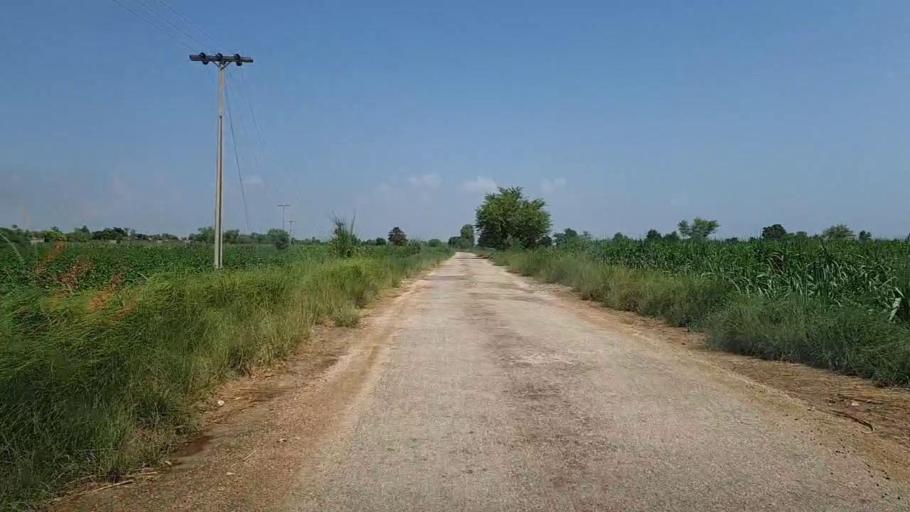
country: PK
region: Sindh
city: Bhiria
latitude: 26.8782
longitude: 68.2448
